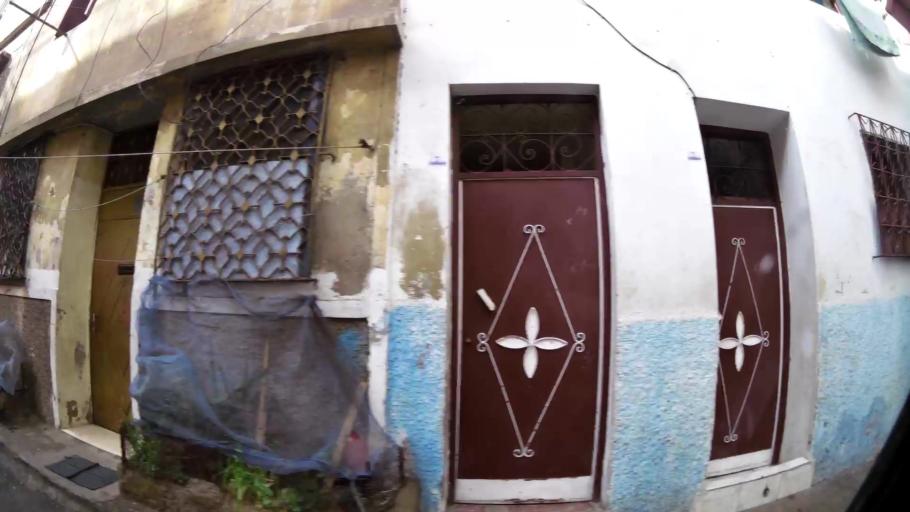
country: MA
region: Grand Casablanca
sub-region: Casablanca
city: Casablanca
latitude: 33.5684
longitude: -7.5842
